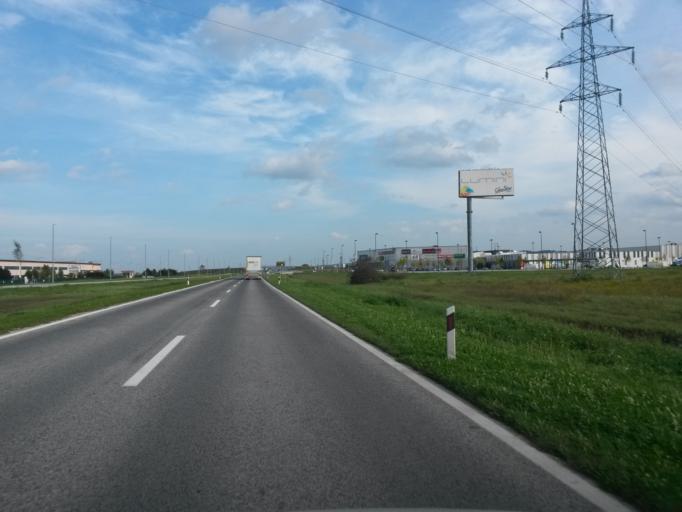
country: HR
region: Varazdinska
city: Varazdin
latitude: 46.2655
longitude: 16.3709
